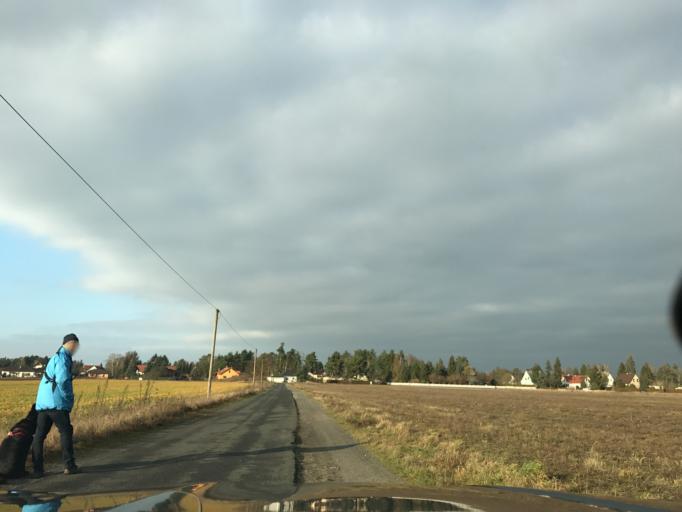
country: DE
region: Brandenburg
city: Brandenburg an der Havel
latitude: 52.3687
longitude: 12.5349
